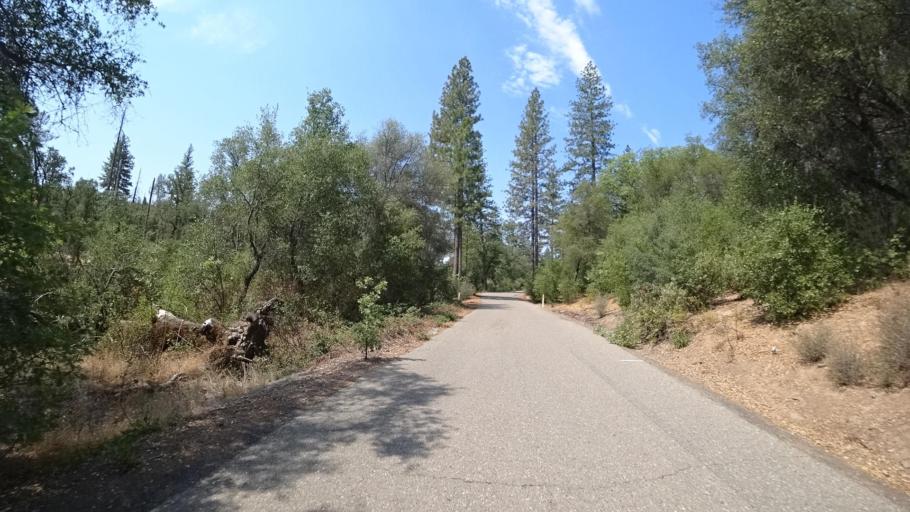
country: US
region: California
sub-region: Mariposa County
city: Midpines
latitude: 37.6955
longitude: -120.1028
